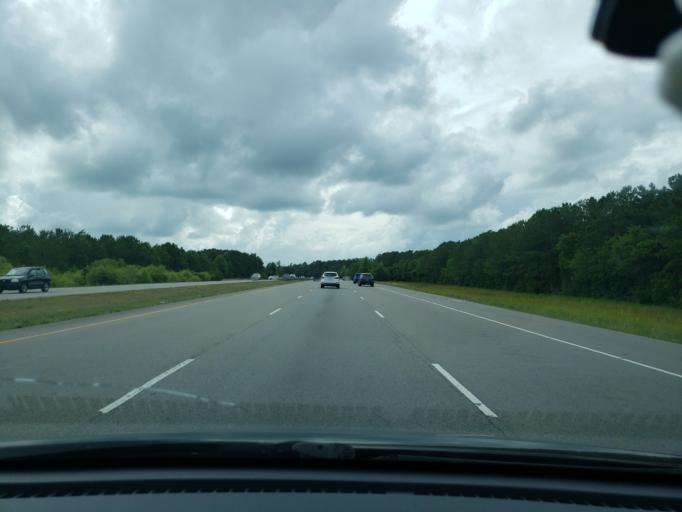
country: US
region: North Carolina
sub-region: New Hanover County
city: Wrightsboro
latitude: 34.2552
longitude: -77.9025
